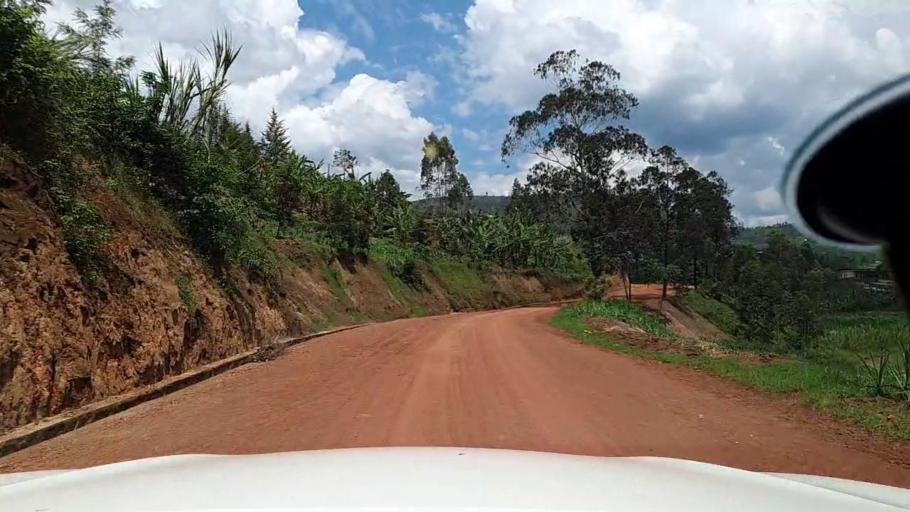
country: RW
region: Northern Province
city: Musanze
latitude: -1.6939
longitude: 29.8197
